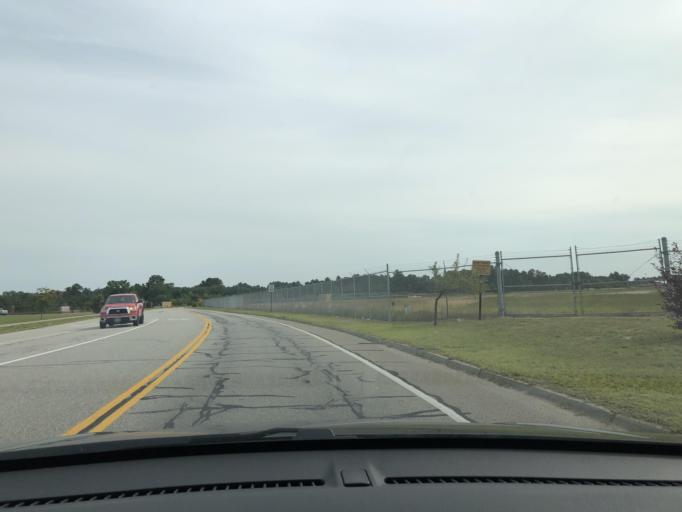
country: US
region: New Hampshire
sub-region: Merrimack County
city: Concord
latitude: 43.2069
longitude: -71.5103
